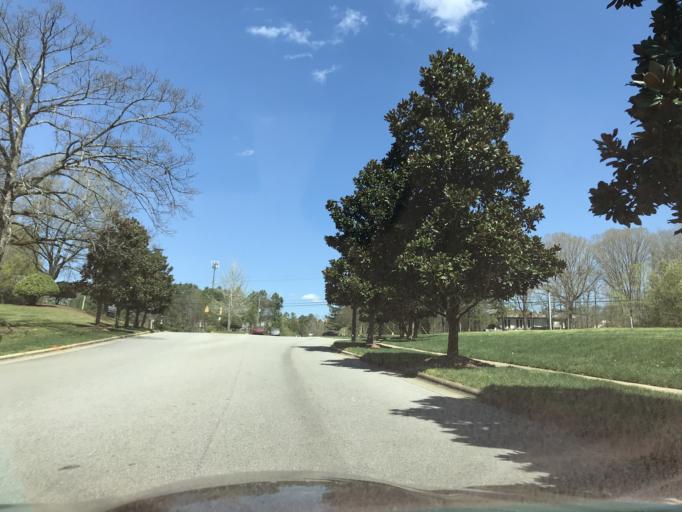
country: US
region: North Carolina
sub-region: Wake County
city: West Raleigh
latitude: 35.8649
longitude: -78.7174
